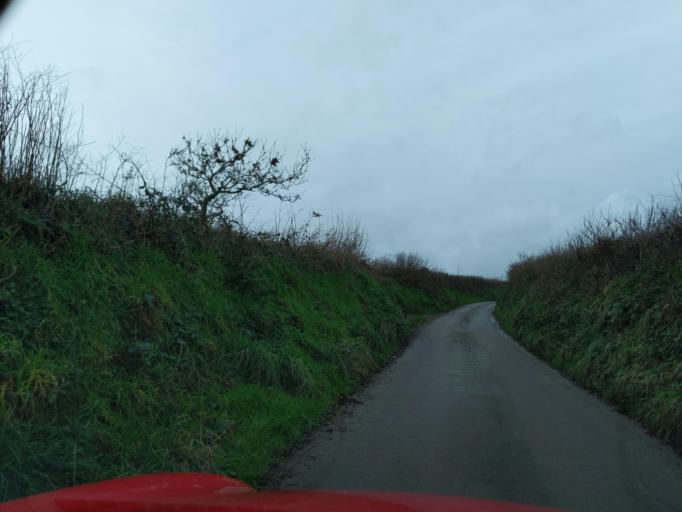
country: GB
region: England
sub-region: Cornwall
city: Duloe
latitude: 50.3456
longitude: -4.5312
